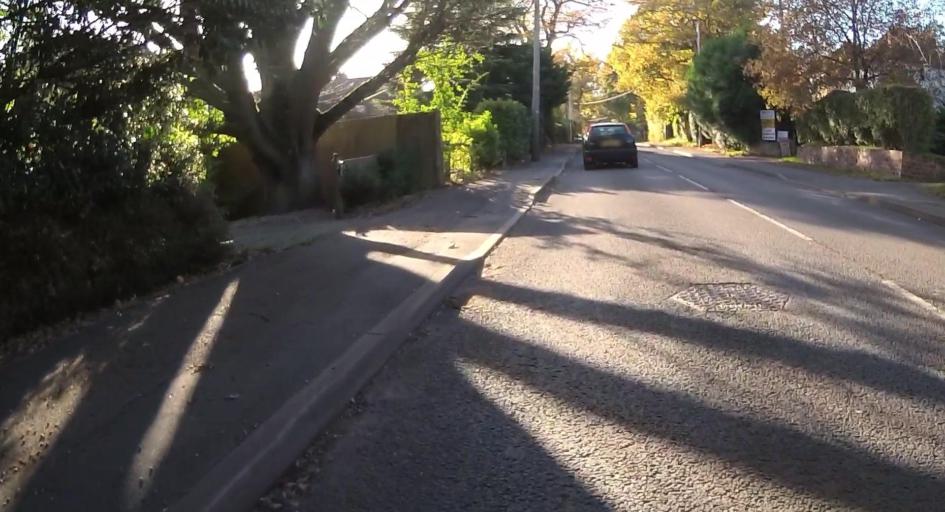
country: GB
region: England
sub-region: Wokingham
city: Barkham
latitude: 51.4033
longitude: -0.8617
